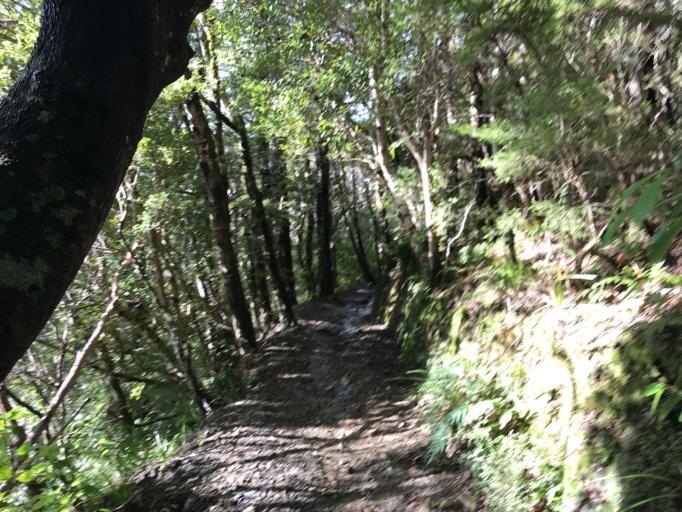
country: NZ
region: Wellington
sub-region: Masterton District
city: Masterton
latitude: -40.9034
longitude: 175.4546
